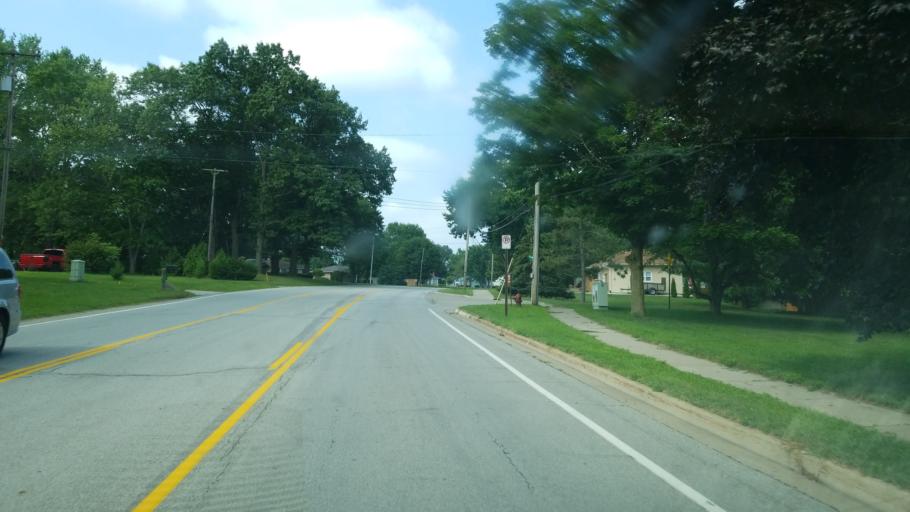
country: US
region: Michigan
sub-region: Kent County
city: Comstock Park
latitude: 43.0299
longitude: -85.6840
